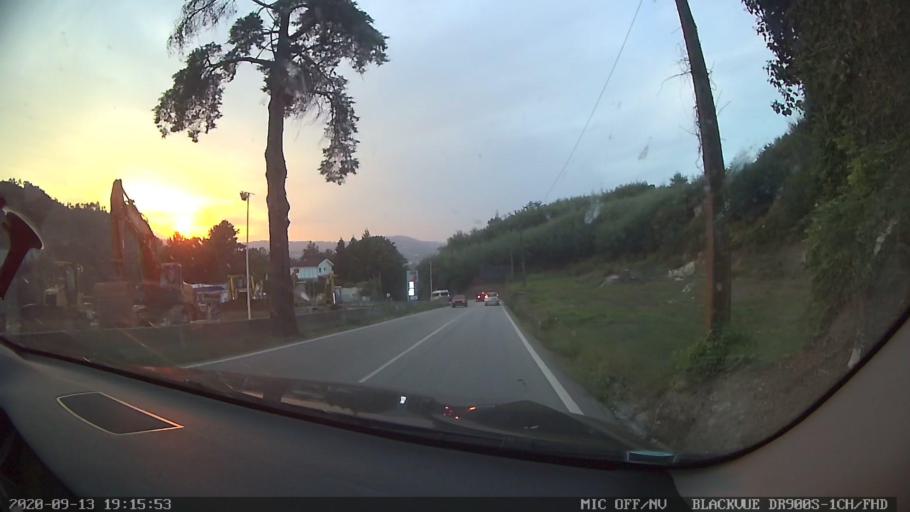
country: PT
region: Porto
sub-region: Amarante
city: Amarante
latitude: 41.2624
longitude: -8.0616
